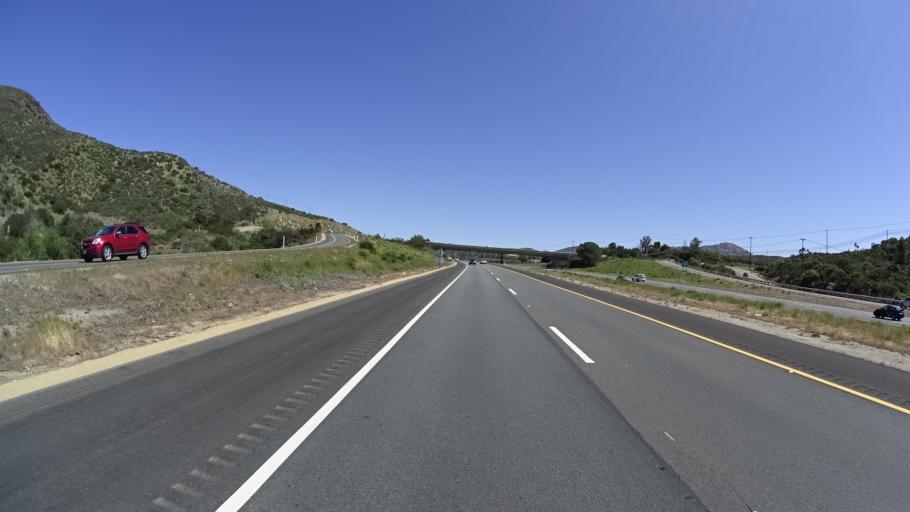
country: US
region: California
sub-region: San Diego County
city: Alpine
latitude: 32.8341
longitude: -116.7336
